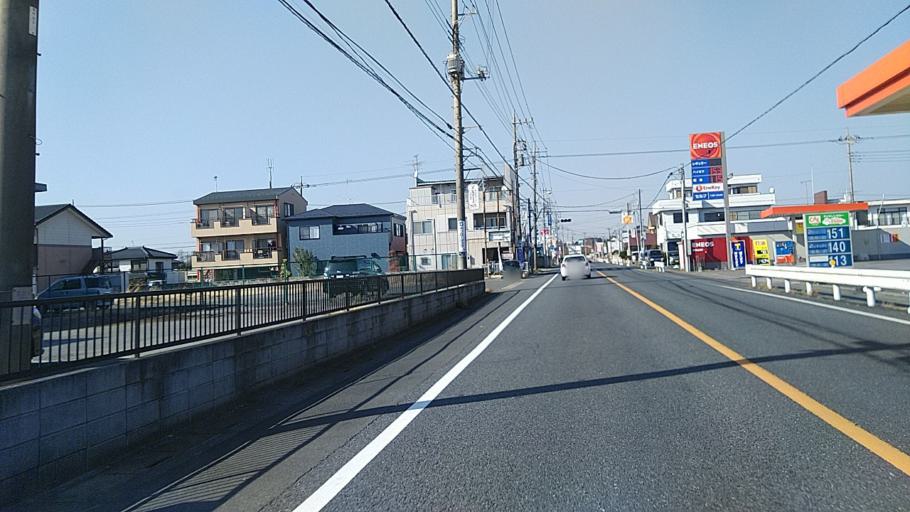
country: JP
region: Saitama
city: Fukiage-fujimi
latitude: 36.0683
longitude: 139.4079
